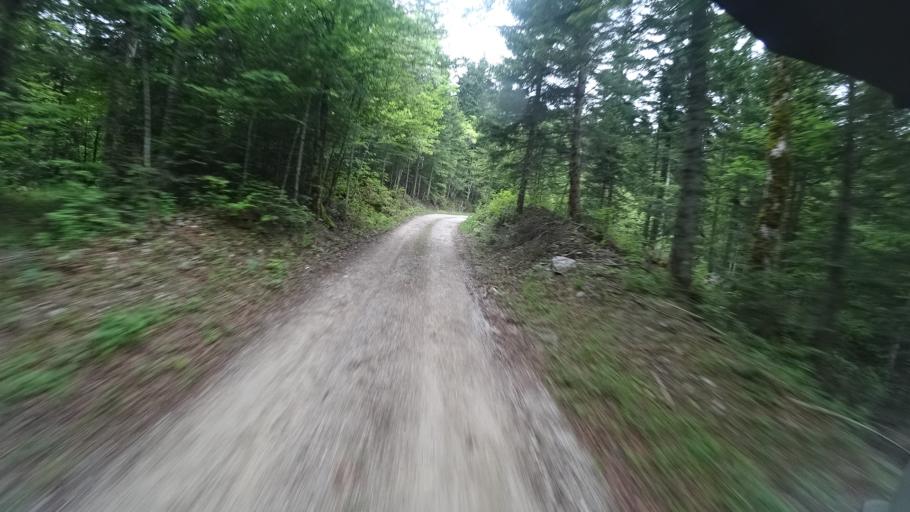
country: BA
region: Federation of Bosnia and Herzegovina
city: Bihac
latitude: 44.6316
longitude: 15.8396
